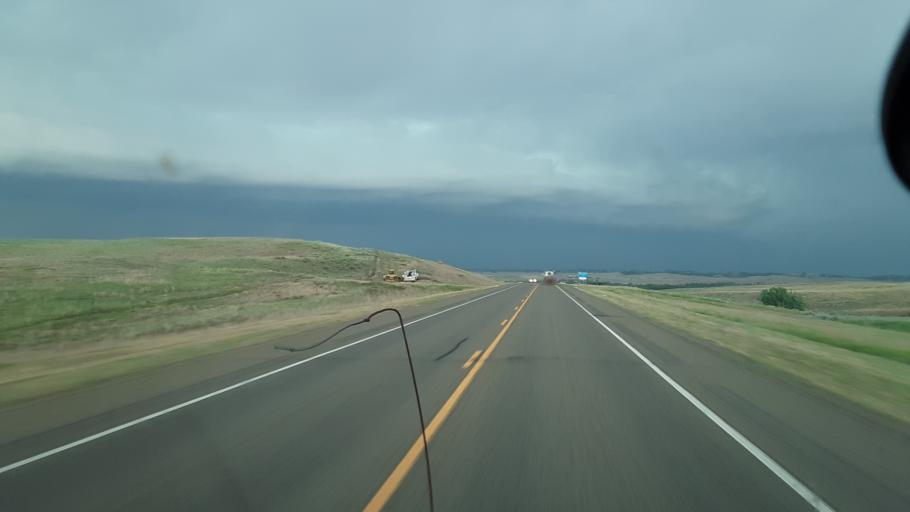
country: US
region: Montana
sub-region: Powder River County
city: Broadus
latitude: 45.4118
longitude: -105.3827
